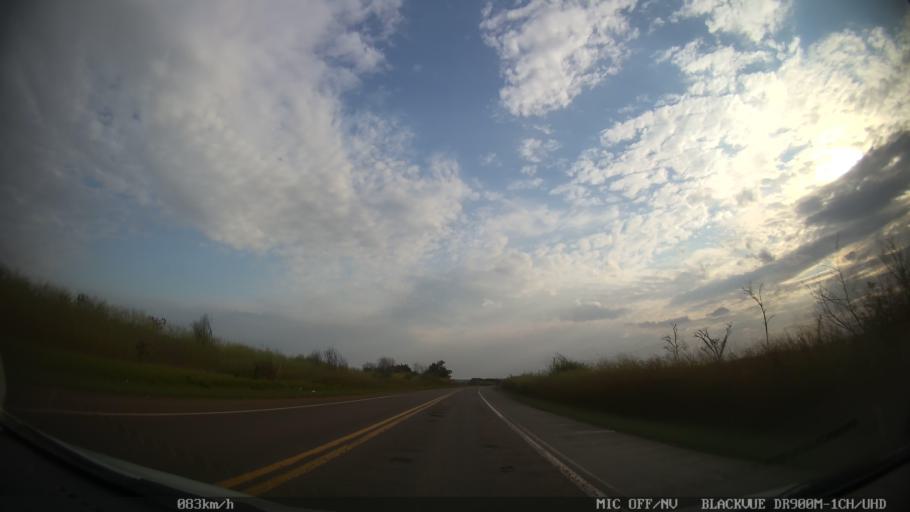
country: BR
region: Sao Paulo
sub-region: Cosmopolis
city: Cosmopolis
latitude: -22.6260
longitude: -47.2606
